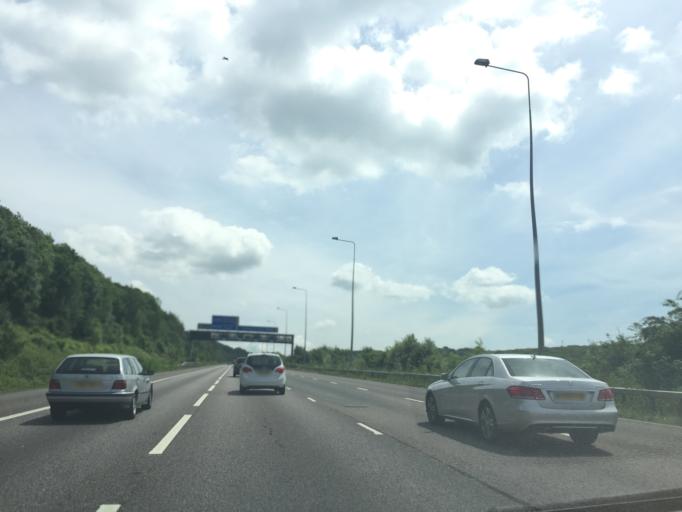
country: GB
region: England
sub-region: Medway
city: Rochester
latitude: 51.3525
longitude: 0.4978
